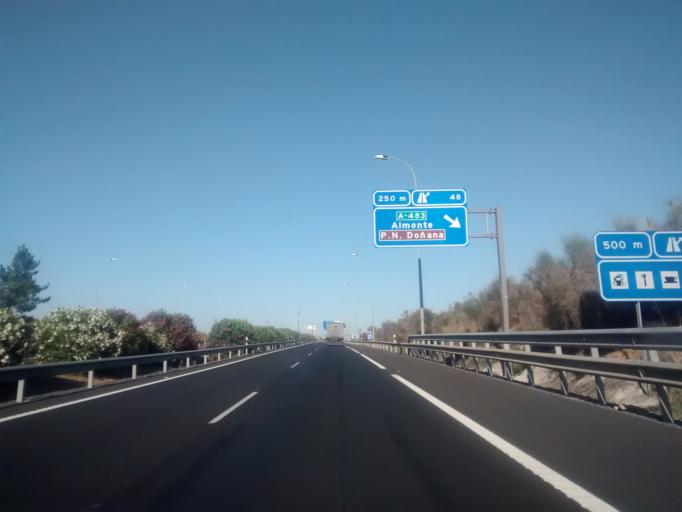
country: ES
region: Andalusia
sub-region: Provincia de Huelva
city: Bollullos par del Condado
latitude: 37.3593
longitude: -6.5315
